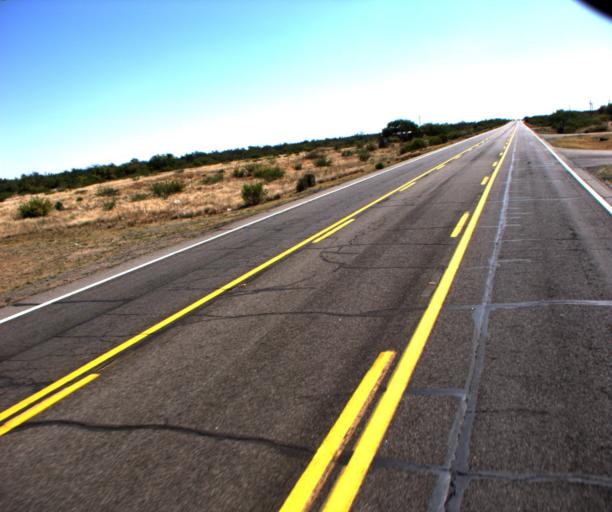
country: US
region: Arizona
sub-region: Pinal County
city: Oracle
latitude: 32.6178
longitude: -110.8153
